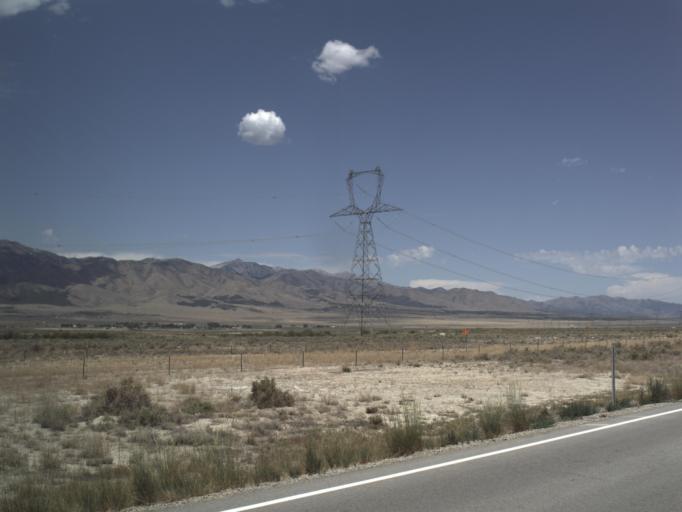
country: US
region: Utah
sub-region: Tooele County
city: Tooele
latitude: 40.3318
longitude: -112.4085
